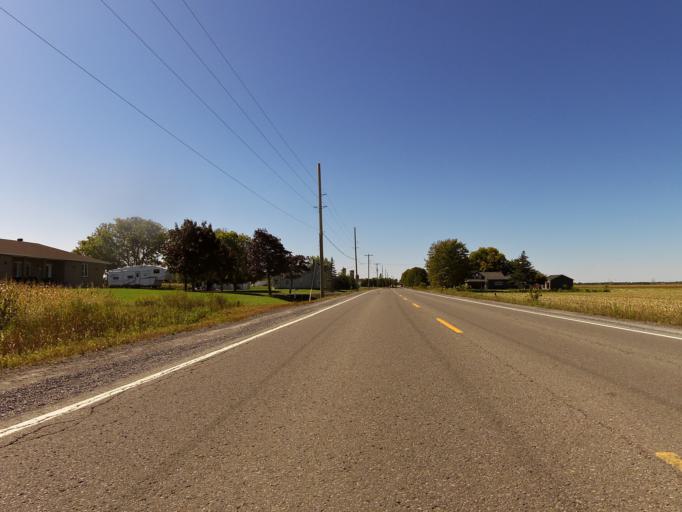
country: CA
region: Ontario
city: Casselman
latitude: 45.2465
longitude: -75.1501
